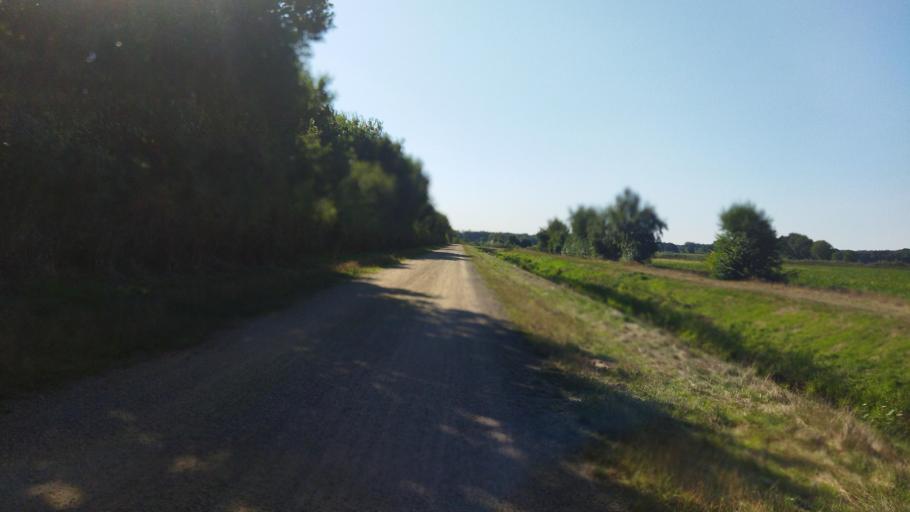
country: DE
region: Lower Saxony
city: Haren
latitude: 52.7795
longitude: 7.2720
